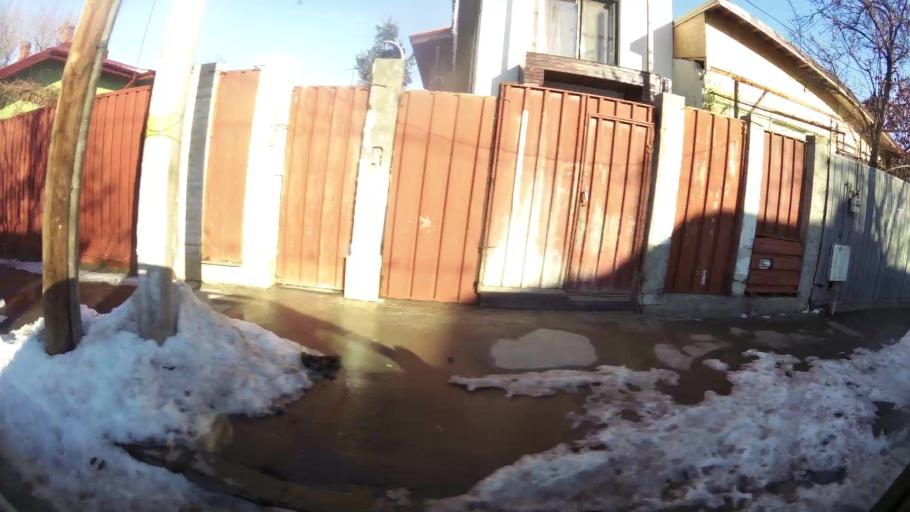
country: RO
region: Bucuresti
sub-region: Municipiul Bucuresti
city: Bucuresti
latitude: 44.4006
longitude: 26.0900
